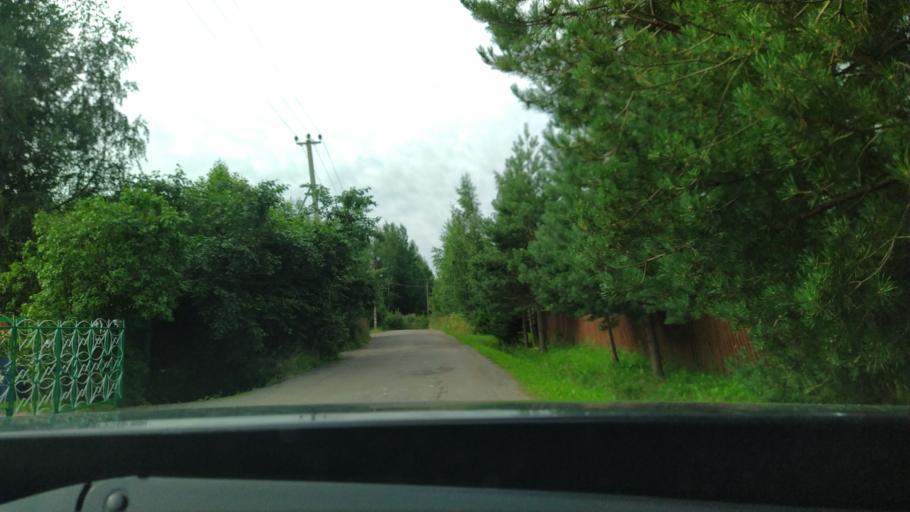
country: RU
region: Leningrad
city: Otradnoye
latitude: 59.7288
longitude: 30.8467
